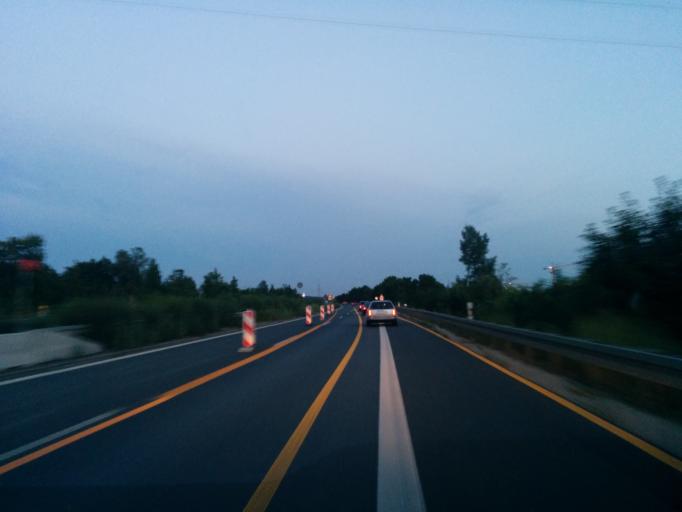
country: DE
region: Bavaria
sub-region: Upper Franconia
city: Forchheim
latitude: 49.7111
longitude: 11.0542
